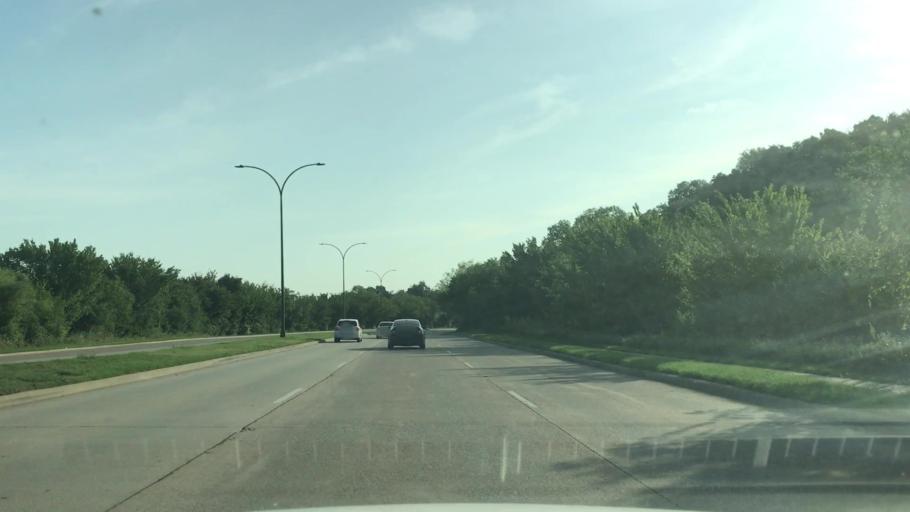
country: US
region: Texas
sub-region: Tarrant County
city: Arlington
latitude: 32.7805
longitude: -97.1229
